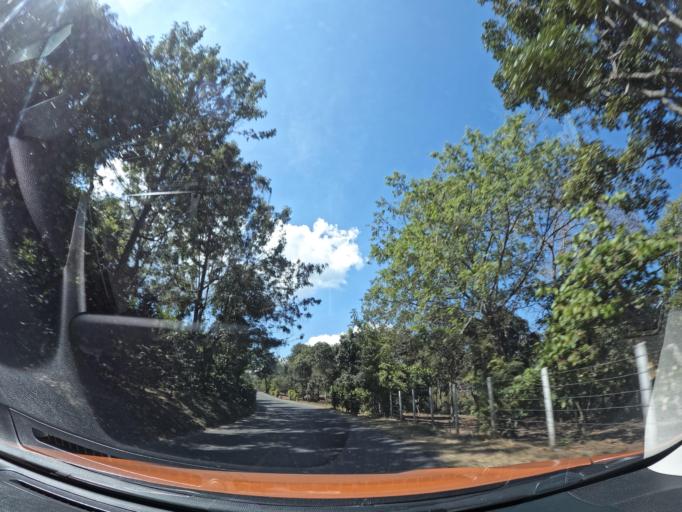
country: GT
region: Solola
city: Santiago Atitlan
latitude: 14.6601
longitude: -91.1820
